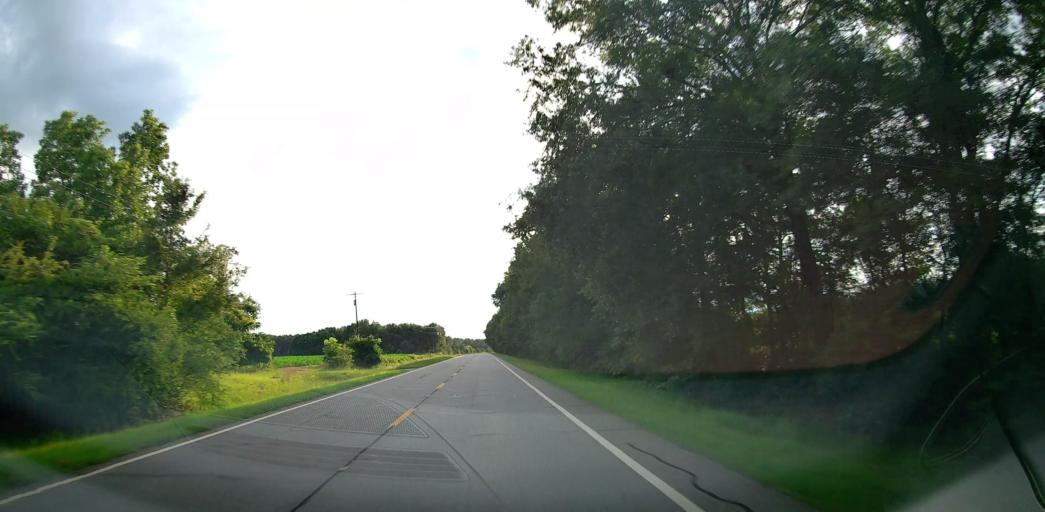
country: US
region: Georgia
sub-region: Pulaski County
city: Hawkinsville
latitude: 32.2956
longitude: -83.5537
